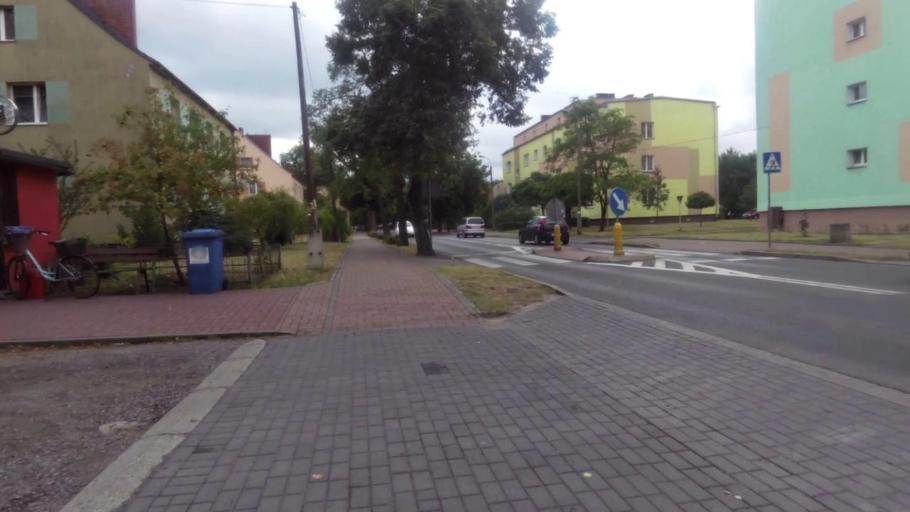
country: PL
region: Lubusz
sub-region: Powiat gorzowski
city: Kostrzyn nad Odra
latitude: 52.5945
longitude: 14.6410
